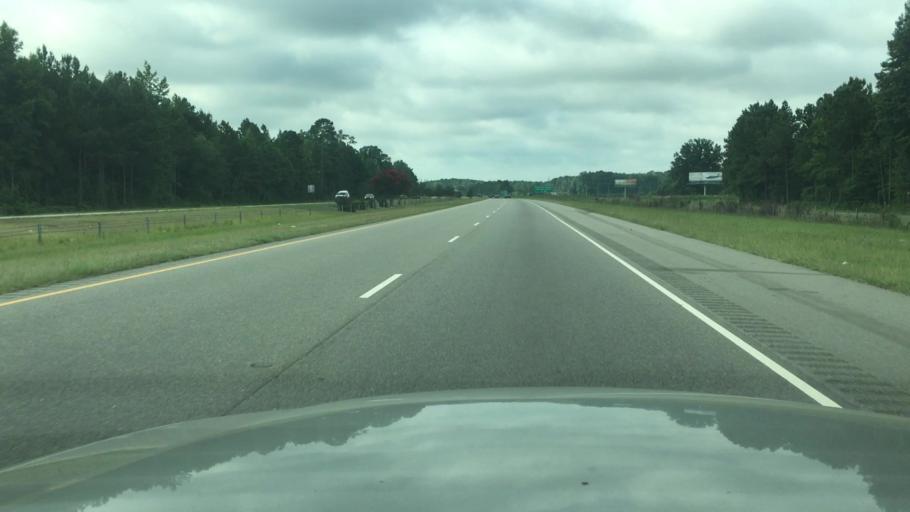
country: US
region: North Carolina
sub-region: Cumberland County
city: Fayetteville
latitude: 35.0202
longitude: -78.8717
